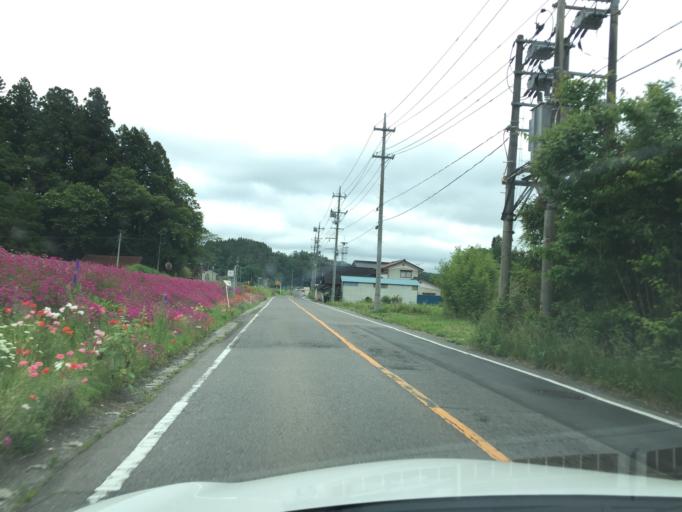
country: JP
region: Fukushima
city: Funehikimachi-funehiki
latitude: 37.4247
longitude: 140.6015
